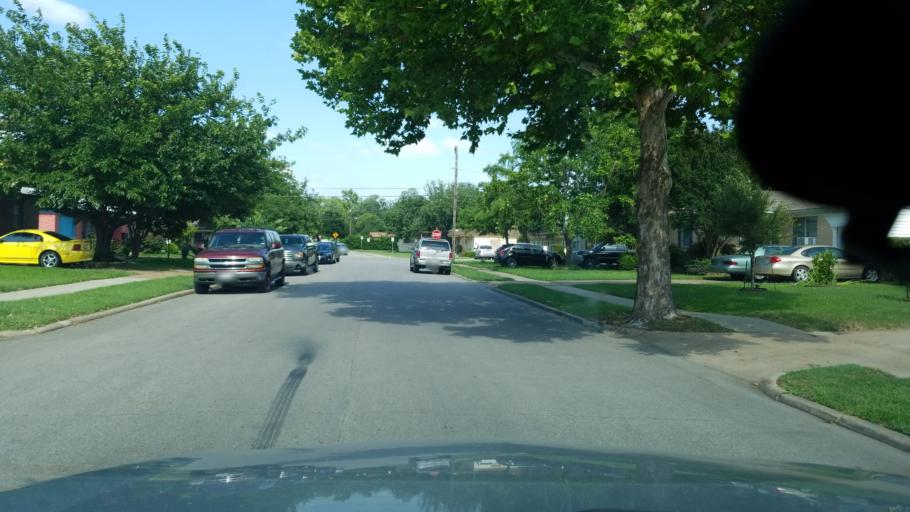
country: US
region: Texas
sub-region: Dallas County
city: Irving
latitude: 32.8180
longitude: -96.9746
